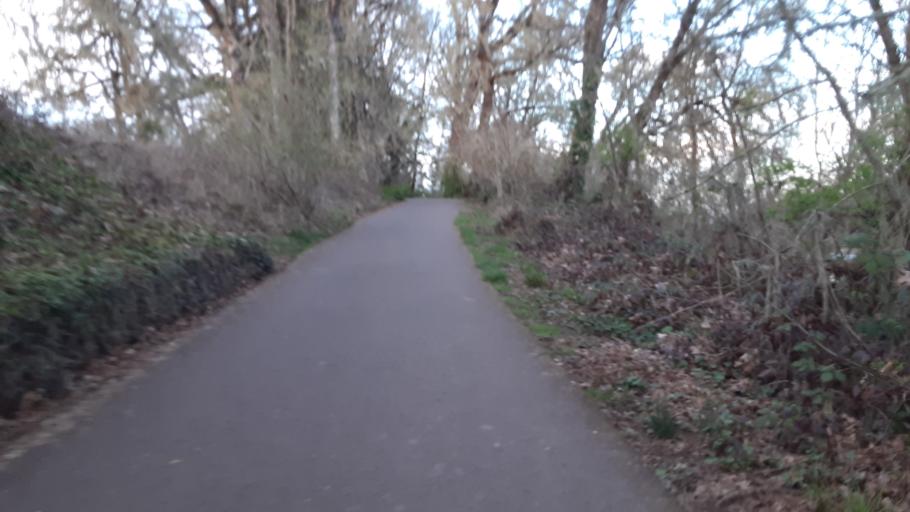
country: US
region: Oregon
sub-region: Benton County
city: Corvallis
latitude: 44.5328
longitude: -123.2514
